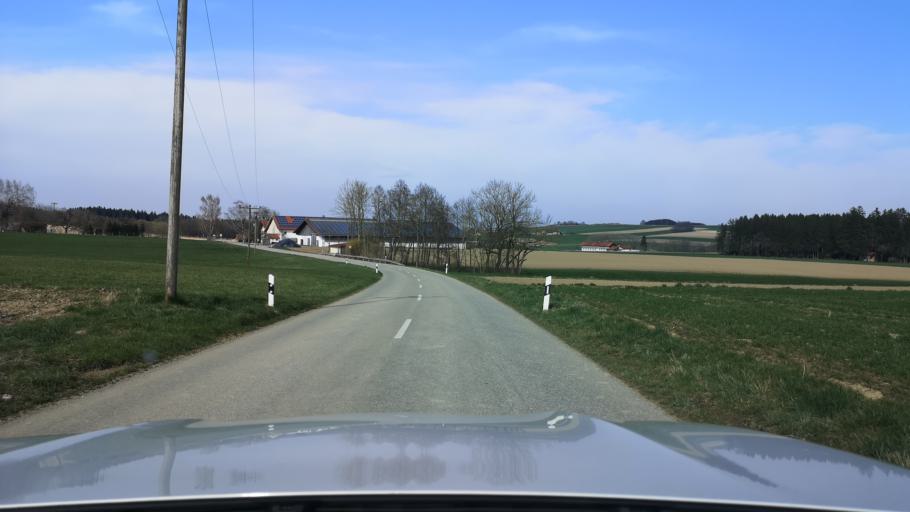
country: DE
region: Bavaria
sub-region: Upper Bavaria
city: Isen
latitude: 48.1614
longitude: 12.0472
